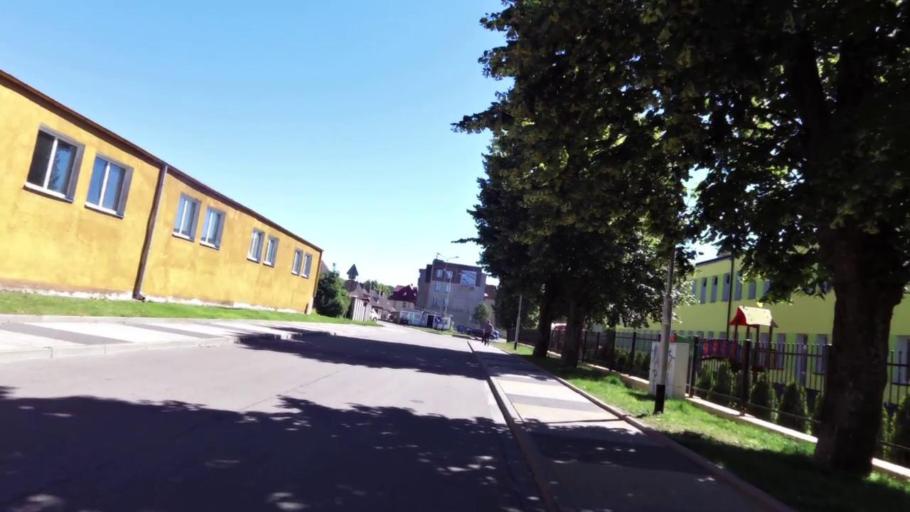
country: PL
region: West Pomeranian Voivodeship
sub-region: Powiat bialogardzki
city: Karlino
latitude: 54.0383
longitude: 15.8795
